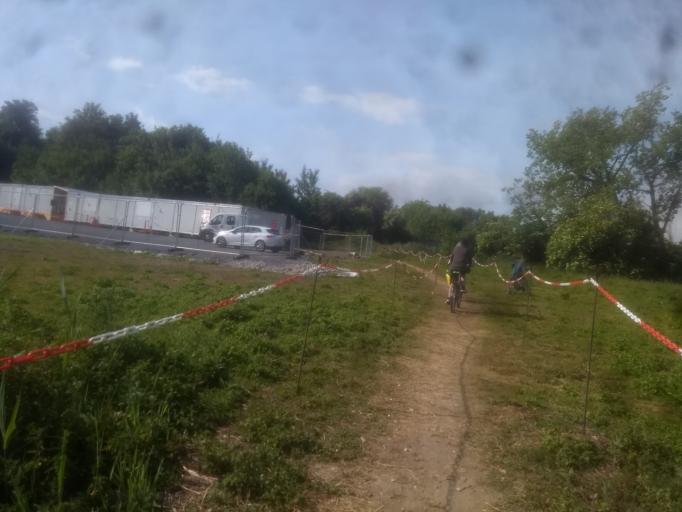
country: FR
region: Nord-Pas-de-Calais
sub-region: Departement du Pas-de-Calais
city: Feuchy
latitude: 50.3028
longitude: 2.8257
